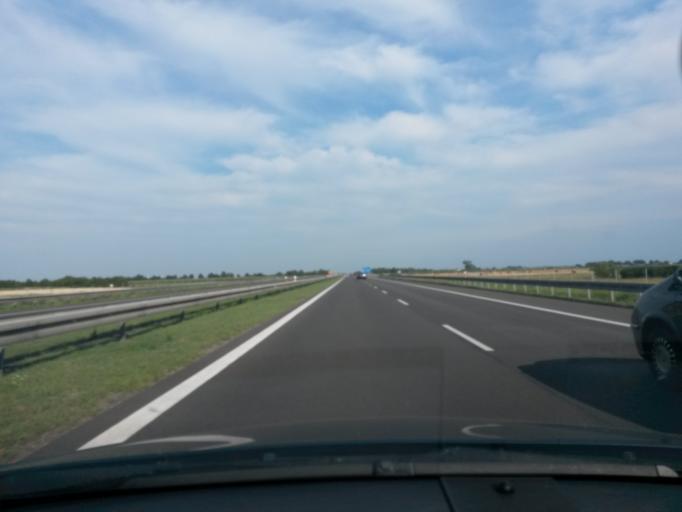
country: PL
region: Greater Poland Voivodeship
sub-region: Powiat slupecki
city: Ladek
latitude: 52.2115
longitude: 17.9907
